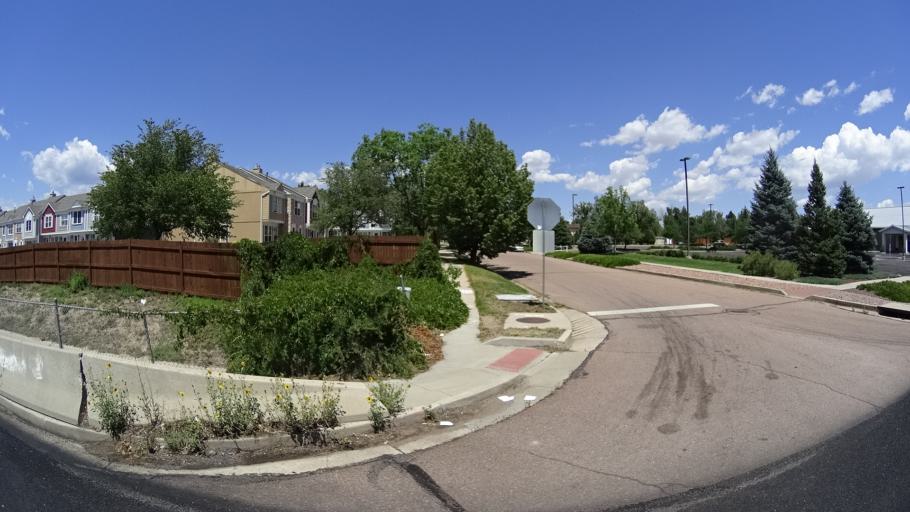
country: US
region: Colorado
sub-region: El Paso County
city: Stratmoor
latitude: 38.7891
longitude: -104.7493
